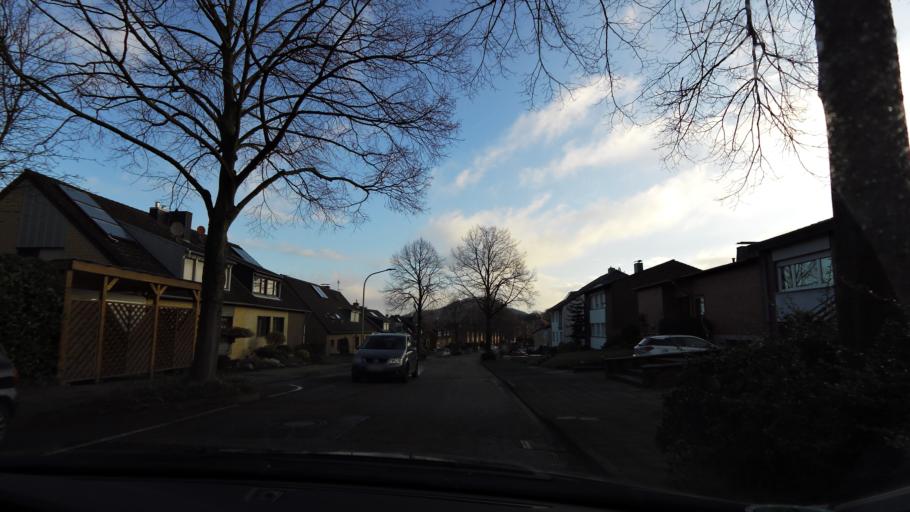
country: DE
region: North Rhine-Westphalia
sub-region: Regierungsbezirk Koln
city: Herzogenrath
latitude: 50.8803
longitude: 6.0963
